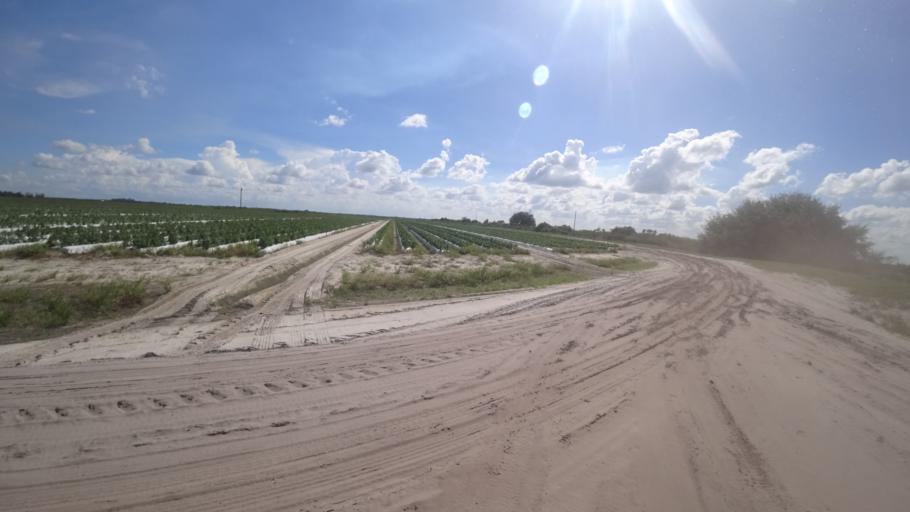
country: US
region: Florida
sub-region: DeSoto County
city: Arcadia
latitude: 27.3440
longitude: -82.0964
